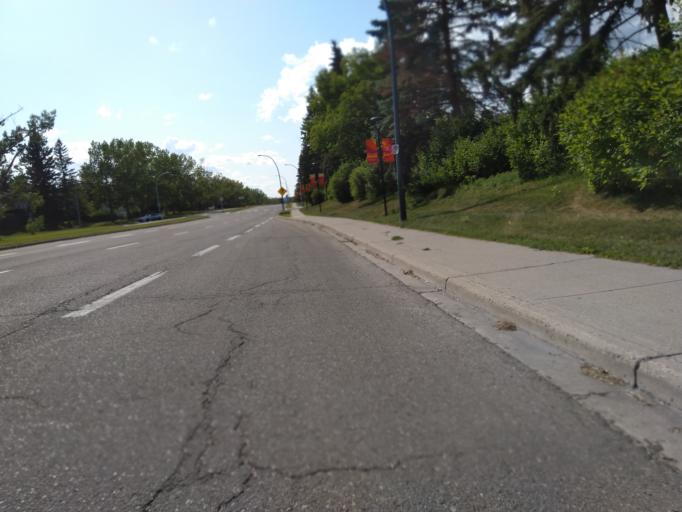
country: CA
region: Alberta
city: Calgary
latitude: 51.0745
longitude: -114.1298
